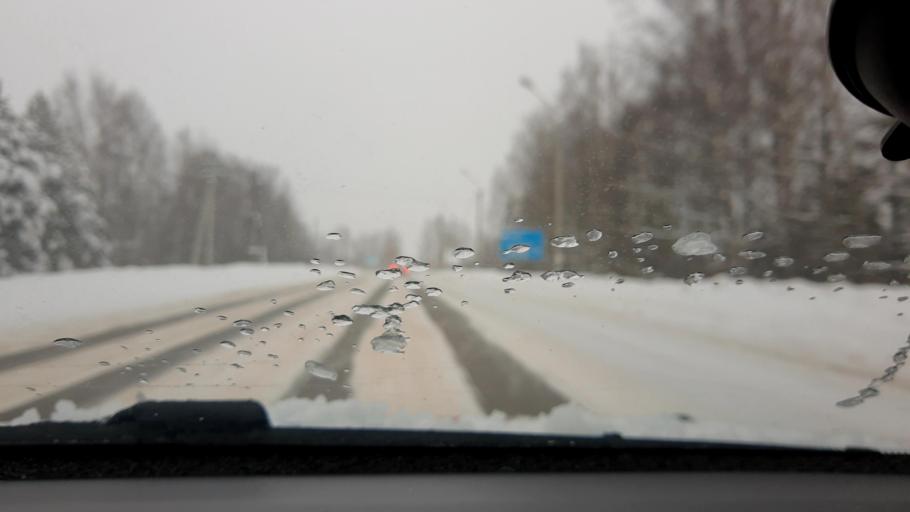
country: RU
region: Nizjnij Novgorod
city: Purekh
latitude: 56.6493
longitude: 43.0857
